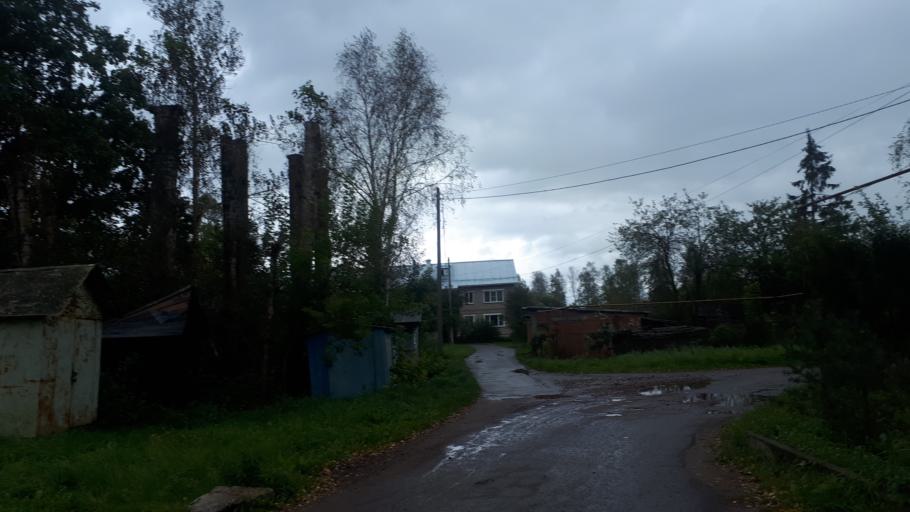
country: RU
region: Jaroslavl
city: Konstantinovskiy
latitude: 57.8280
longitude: 39.5876
